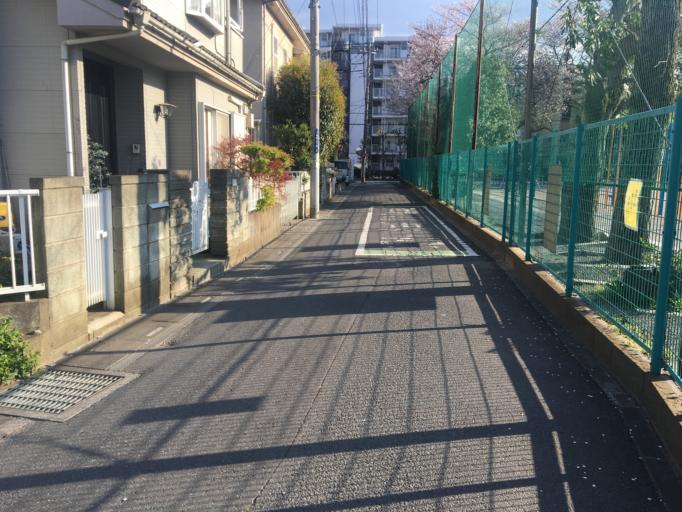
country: JP
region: Saitama
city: Shiki
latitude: 35.8327
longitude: 139.5701
